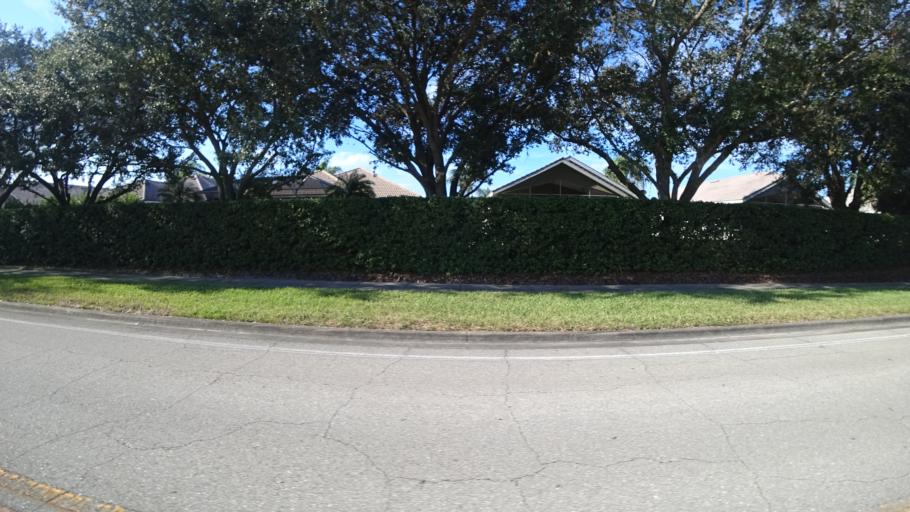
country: US
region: Florida
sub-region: Sarasota County
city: Desoto Lakes
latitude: 27.4197
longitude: -82.4822
